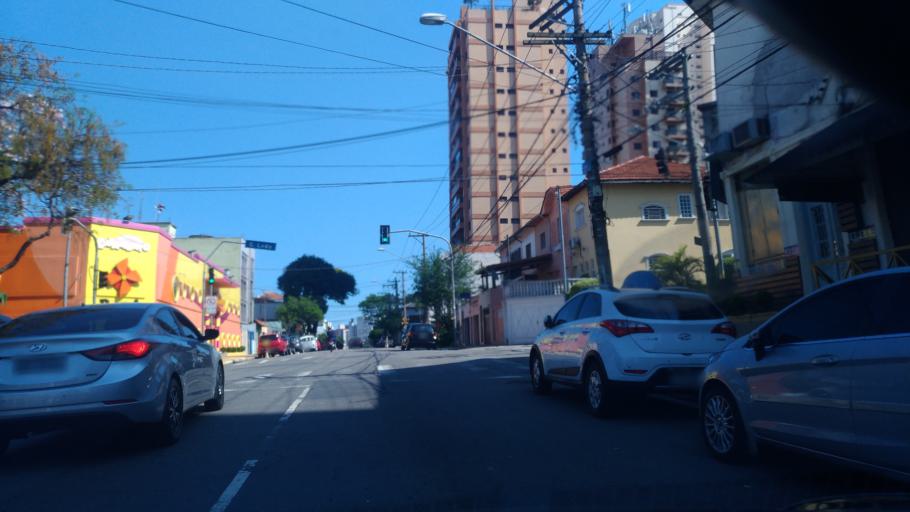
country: BR
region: Sao Paulo
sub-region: Sao Caetano Do Sul
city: Sao Caetano do Sul
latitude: -23.5969
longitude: -46.6032
